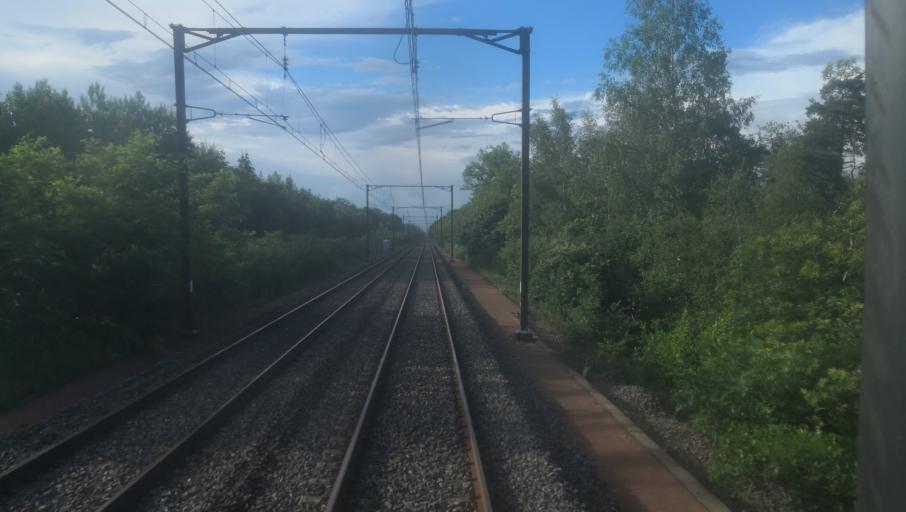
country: FR
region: Centre
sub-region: Departement du Loir-et-Cher
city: Nouan-le-Fuzelier
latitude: 47.4846
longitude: 2.0386
